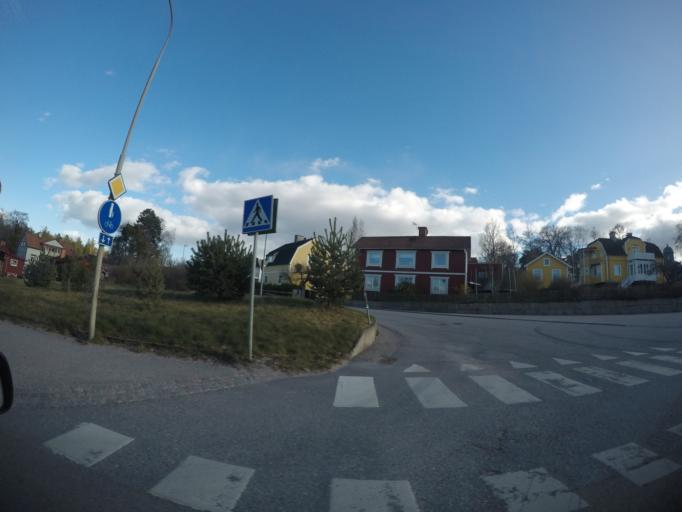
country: SE
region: Vaestmanland
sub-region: Kungsors Kommun
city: Kungsoer
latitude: 59.4263
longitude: 16.0997
